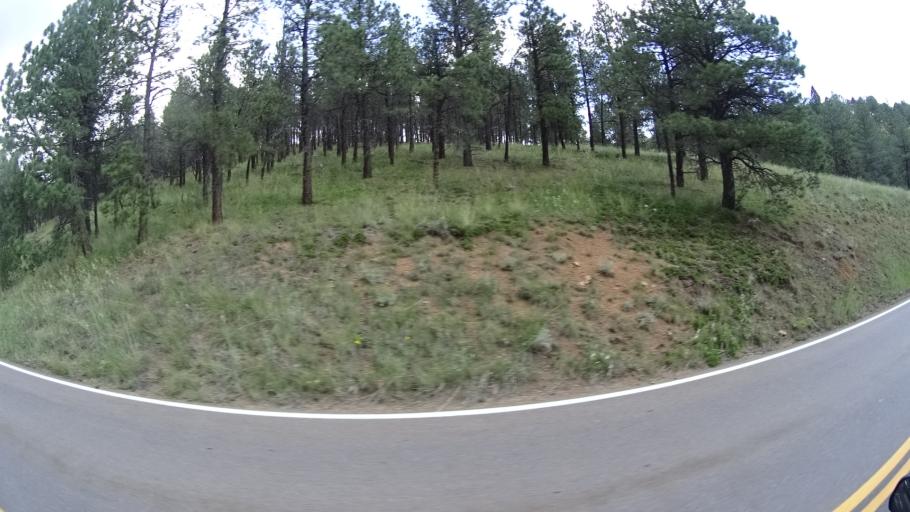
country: US
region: Colorado
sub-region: El Paso County
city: Cascade-Chipita Park
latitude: 38.9120
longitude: -105.0206
